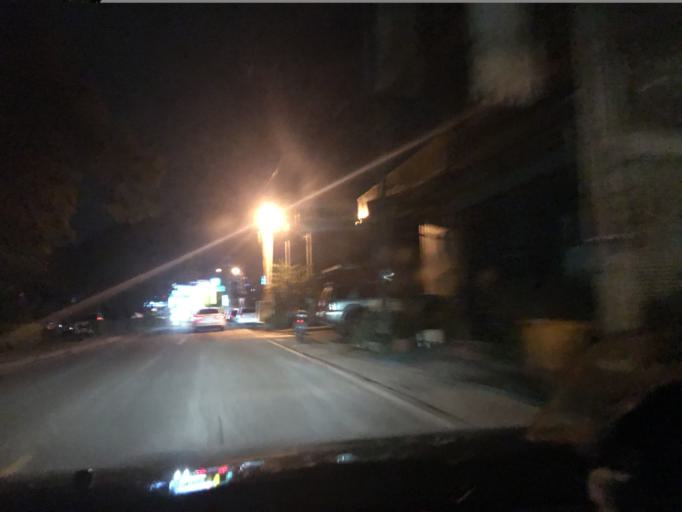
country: TW
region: Taiwan
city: Daxi
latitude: 24.8530
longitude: 121.2200
